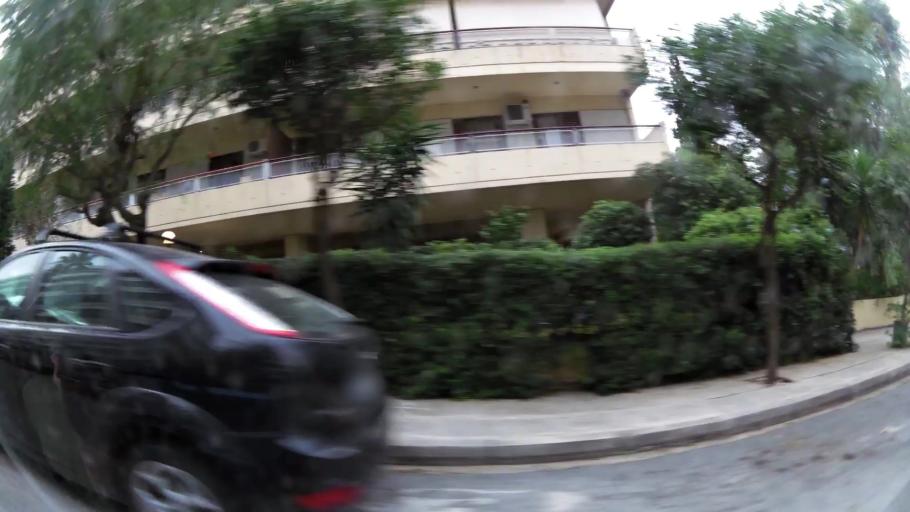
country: GR
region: Attica
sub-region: Nomarchia Athinas
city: Palaio Faliro
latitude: 37.9192
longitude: 23.7056
